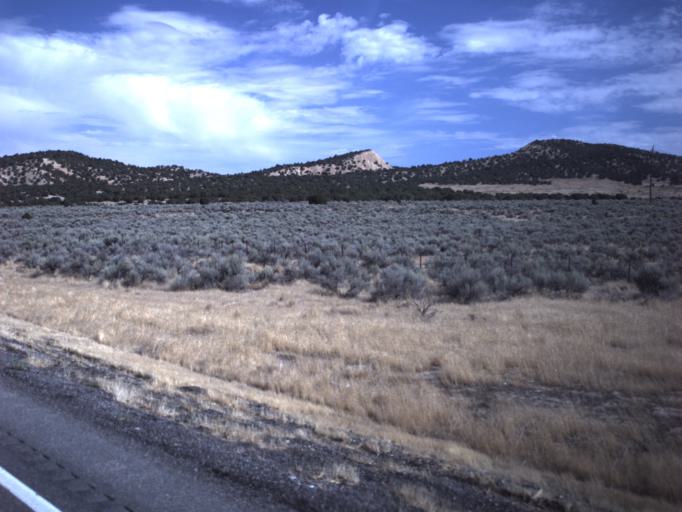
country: US
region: Utah
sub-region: Sanpete County
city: Gunnison
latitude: 39.3430
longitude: -111.9233
